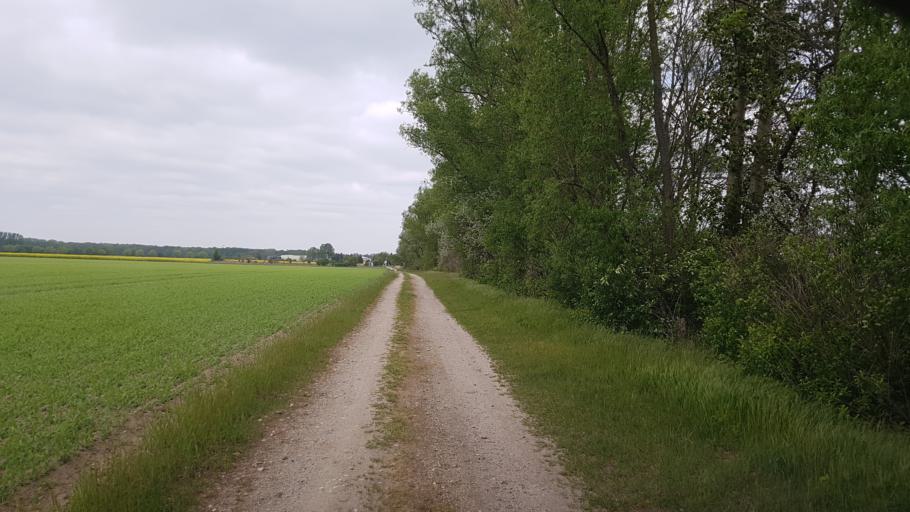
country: DE
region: Brandenburg
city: Sonnewalde
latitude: 51.6834
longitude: 13.6346
